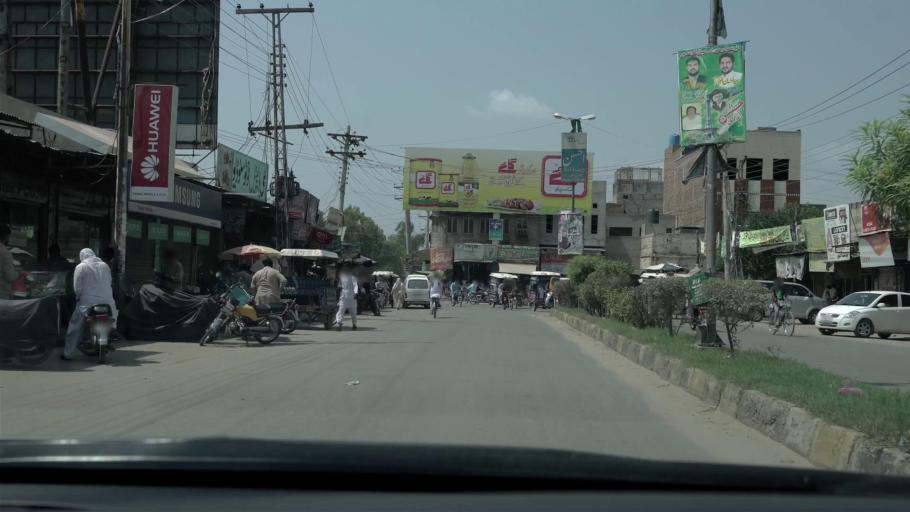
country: PK
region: Punjab
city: Gojra
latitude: 31.1518
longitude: 72.6775
